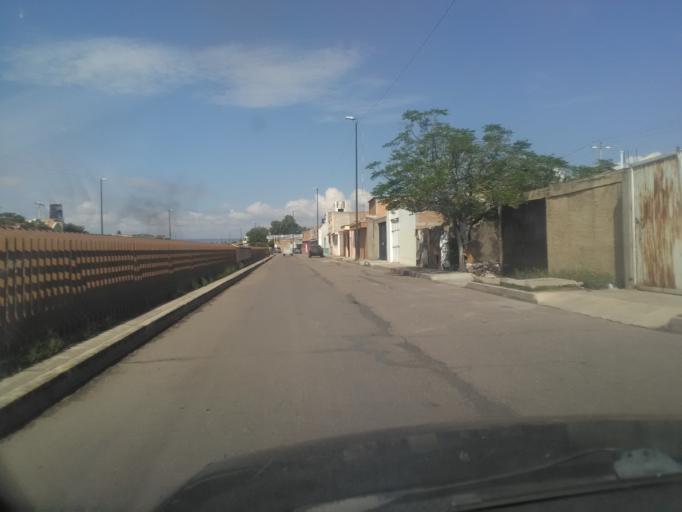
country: MX
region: Durango
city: Victoria de Durango
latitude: 24.0210
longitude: -104.6262
